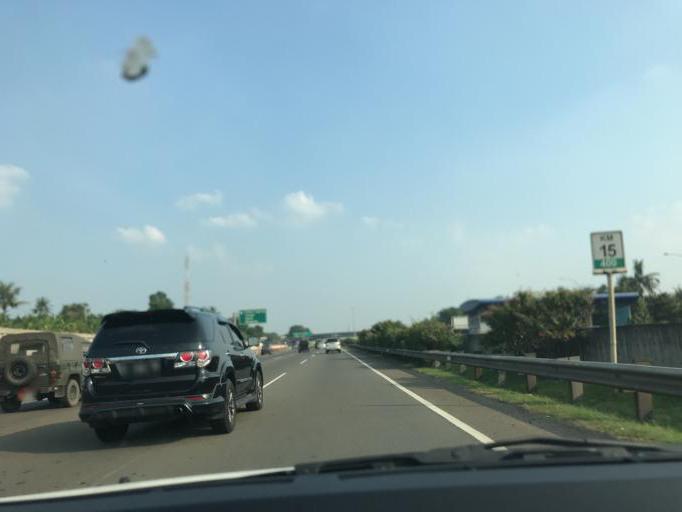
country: ID
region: West Java
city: Cileungsir
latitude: -6.3815
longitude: 106.8961
